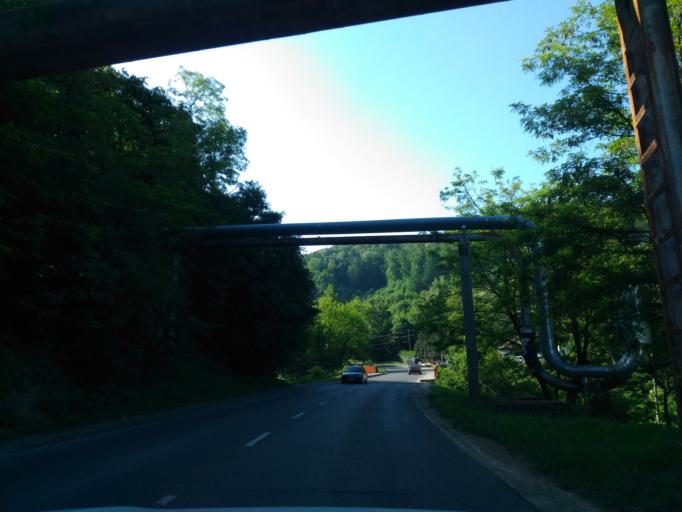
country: HU
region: Baranya
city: Komlo
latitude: 46.1889
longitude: 18.2794
